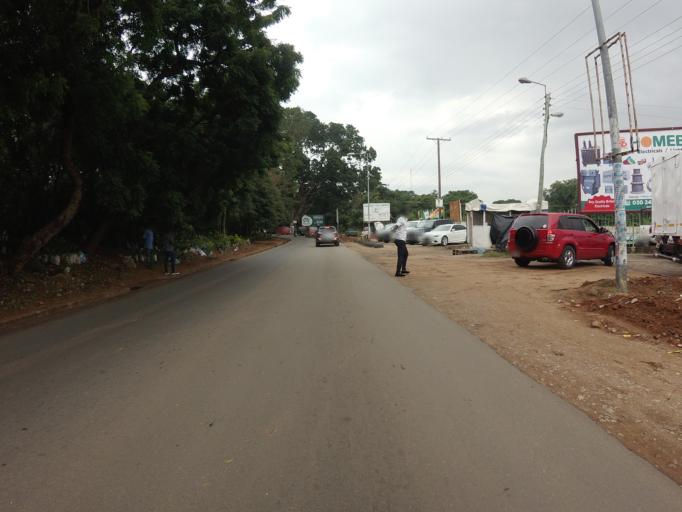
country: GH
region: Greater Accra
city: Dome
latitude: 5.6297
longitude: -0.2199
